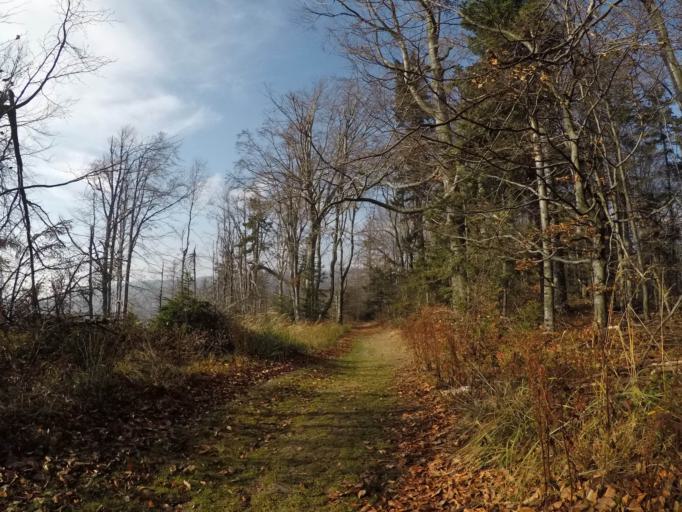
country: SK
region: Kosicky
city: Gelnica
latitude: 48.7640
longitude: 21.0676
